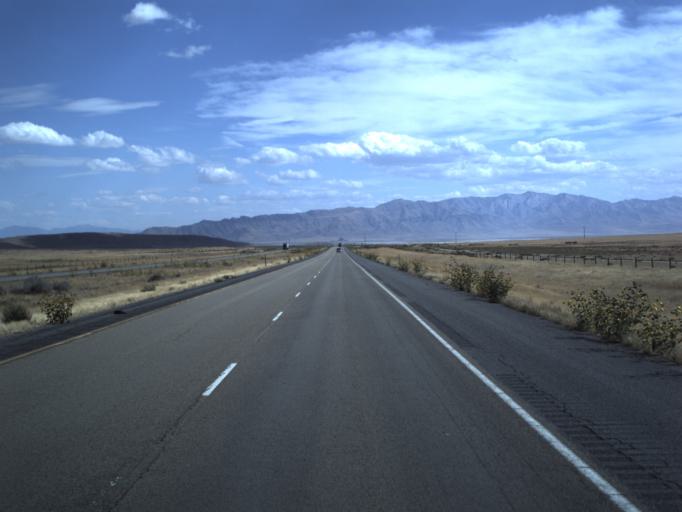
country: US
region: Utah
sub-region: Tooele County
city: Grantsville
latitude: 40.8040
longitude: -112.8570
